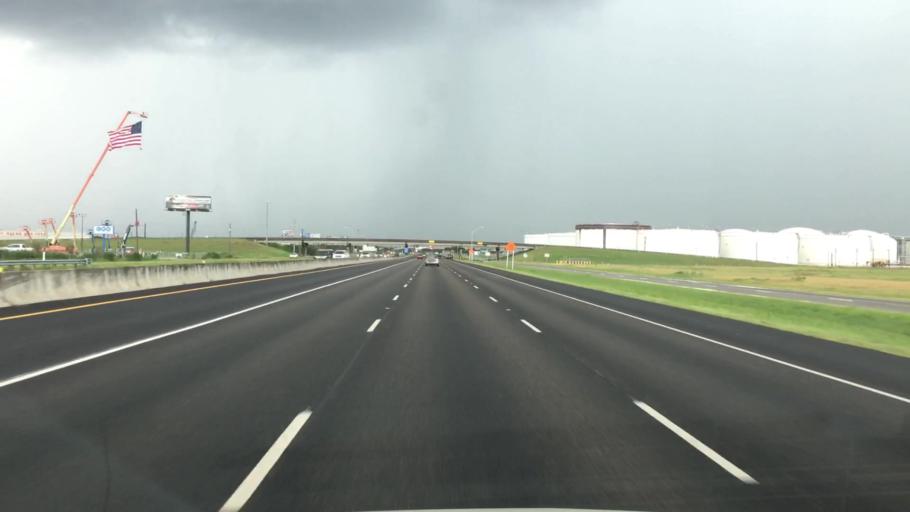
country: US
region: Texas
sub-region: Nueces County
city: Corpus Christi
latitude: 27.8099
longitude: -97.4995
